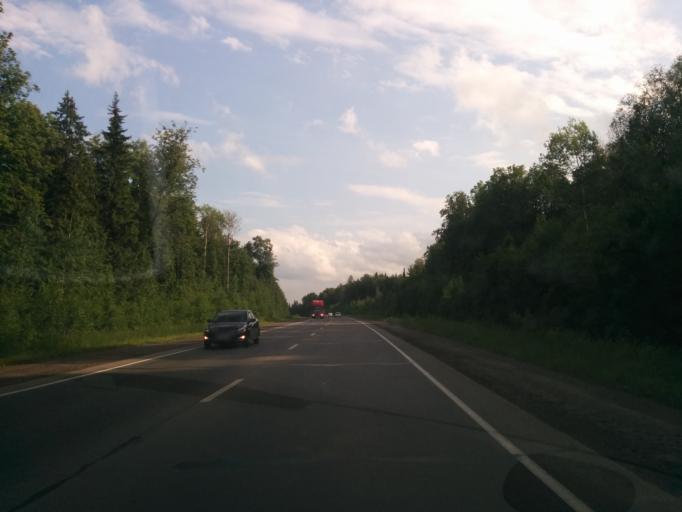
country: RU
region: Perm
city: Polazna
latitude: 58.1015
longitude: 56.4250
